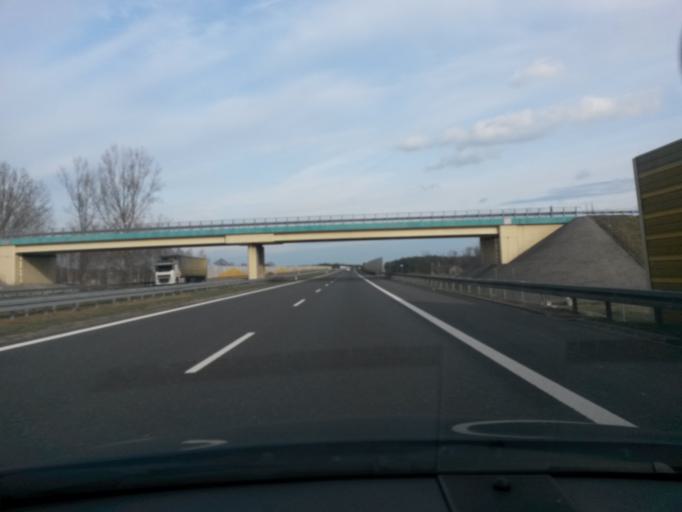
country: PL
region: Lodz Voivodeship
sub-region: Powiat leczycki
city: Swinice Warckie
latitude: 52.0282
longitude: 18.9053
